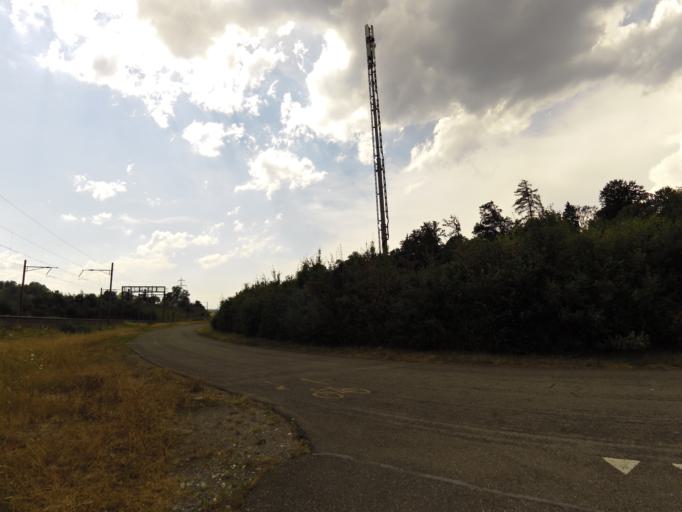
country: CH
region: Aargau
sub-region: Bezirk Lenzburg
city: Othmarsingen
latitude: 47.3941
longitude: 8.2010
